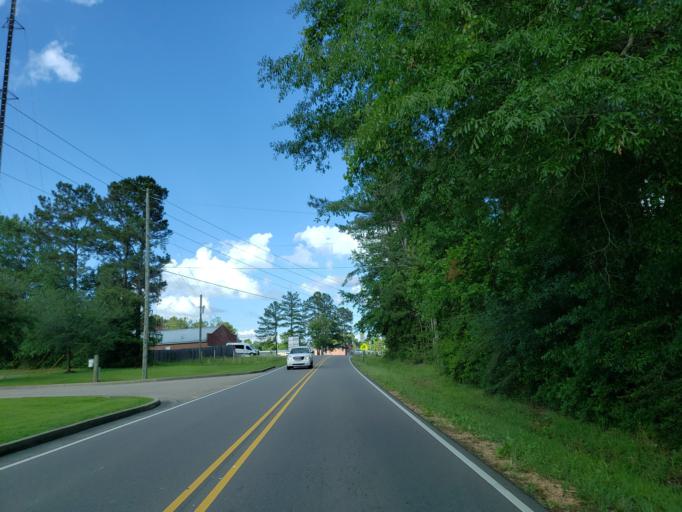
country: US
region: Mississippi
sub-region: Lamar County
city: West Hattiesburg
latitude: 31.2853
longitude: -89.4222
